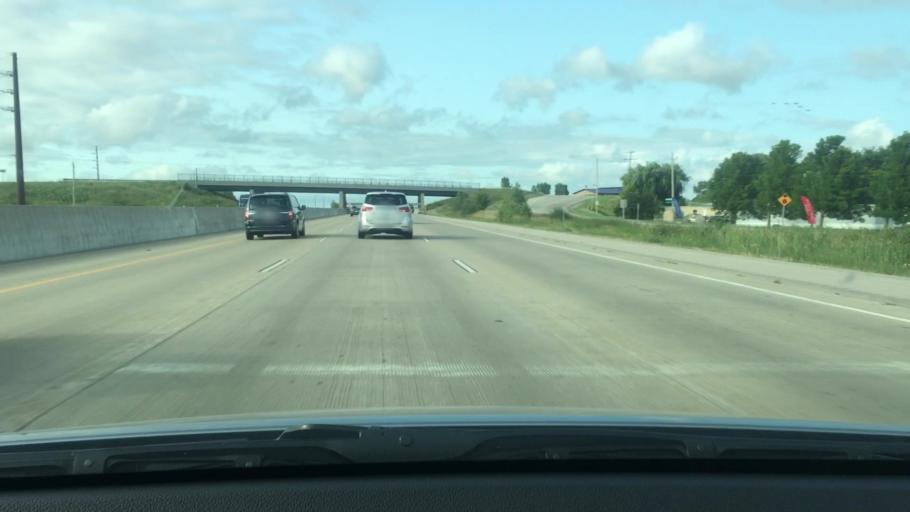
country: US
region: Wisconsin
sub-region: Winnebago County
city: Oshkosh
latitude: 44.0703
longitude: -88.5679
